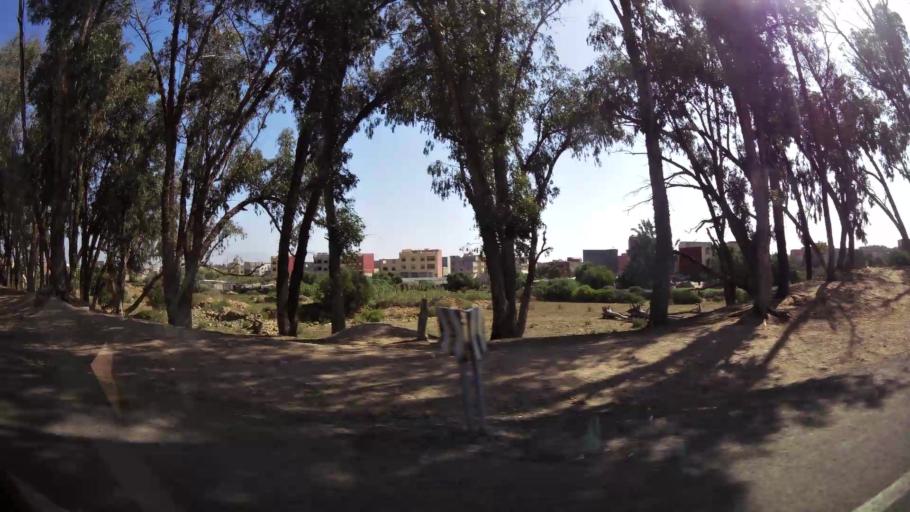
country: MA
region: Souss-Massa-Draa
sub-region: Inezgane-Ait Mellou
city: Inezgane
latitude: 30.3215
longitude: -9.5282
